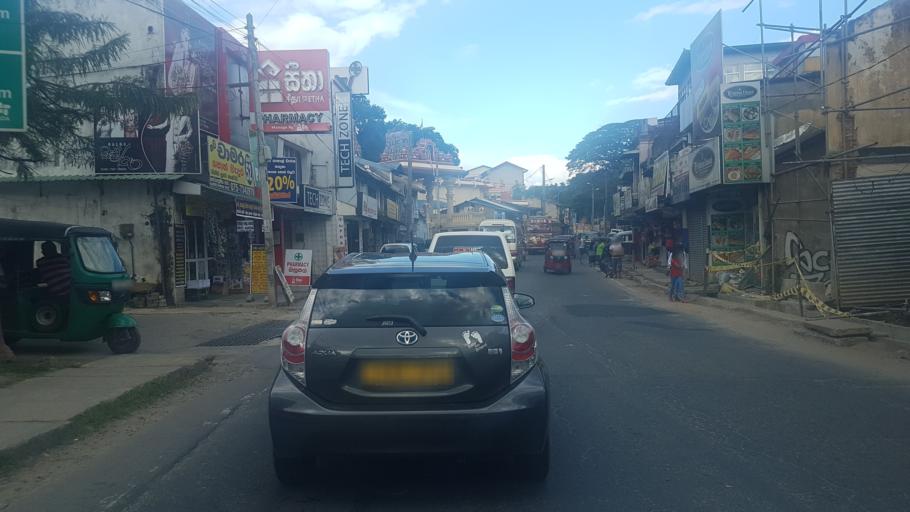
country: LK
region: Central
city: Kandy
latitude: 7.2924
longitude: 80.6320
